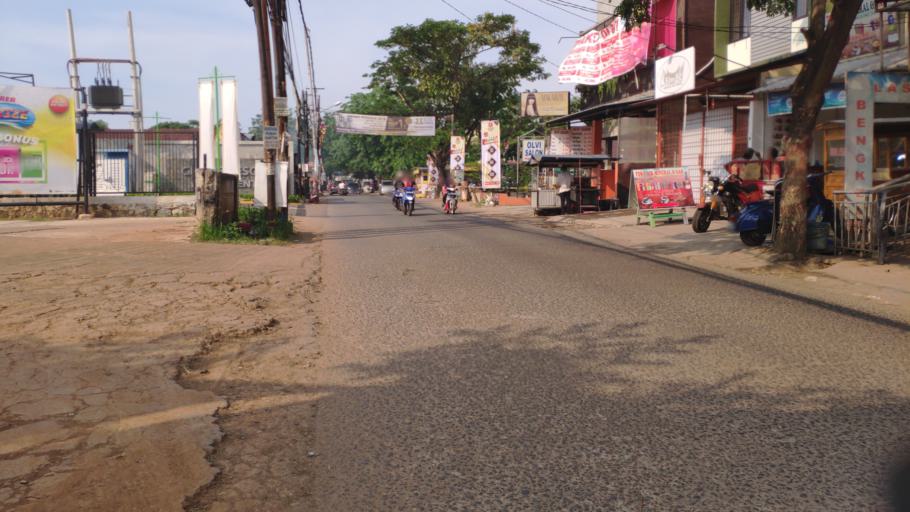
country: ID
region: West Java
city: Pamulang
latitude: -6.3368
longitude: 106.7948
